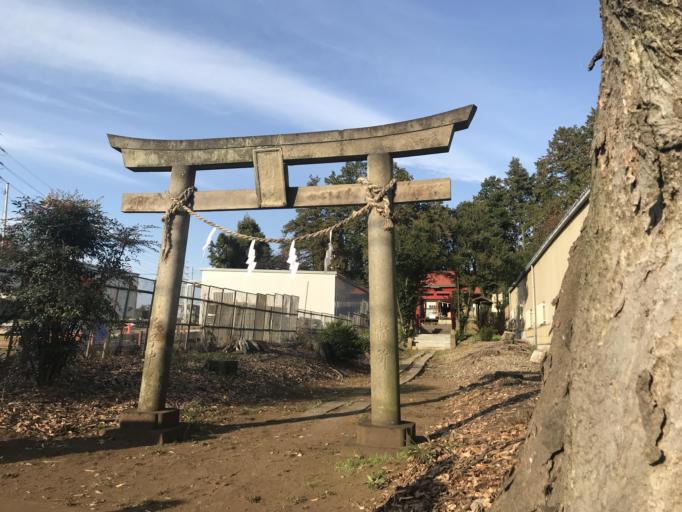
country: JP
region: Saitama
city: Tokorozawa
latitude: 35.8085
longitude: 139.5039
